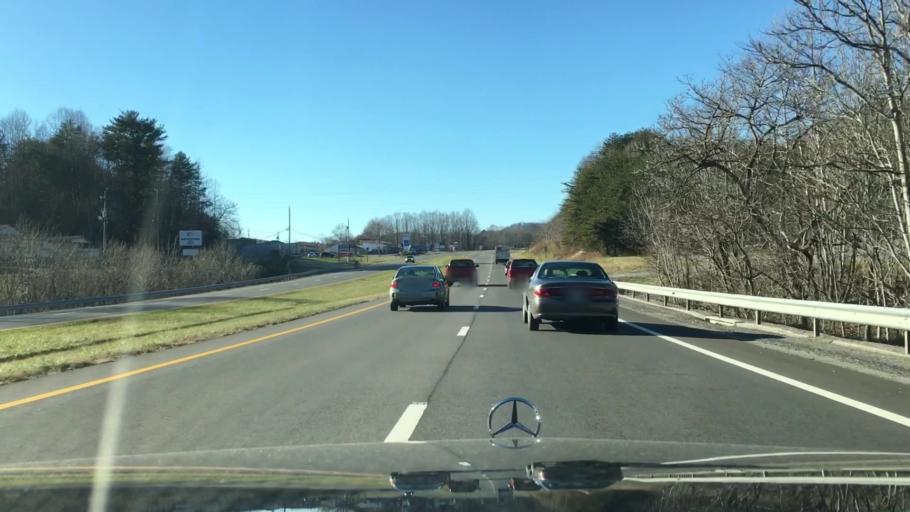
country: US
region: Virginia
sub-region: Roanoke County
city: Vinton
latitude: 37.2708
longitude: -79.8036
